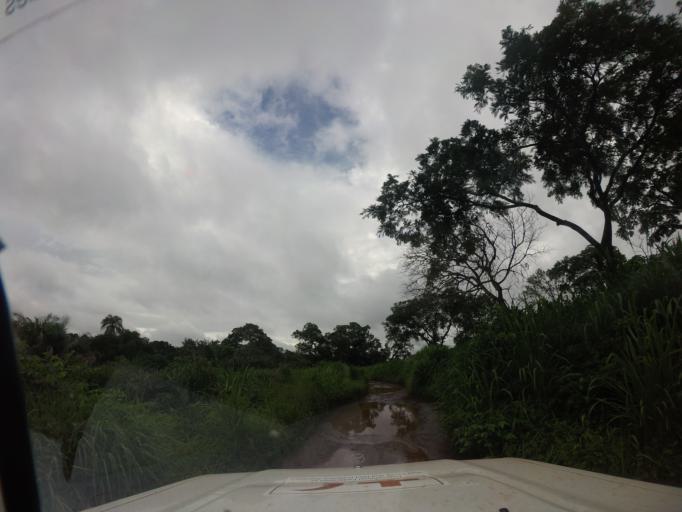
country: SL
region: Northern Province
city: Kamakwie
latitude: 9.6618
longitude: -12.2182
